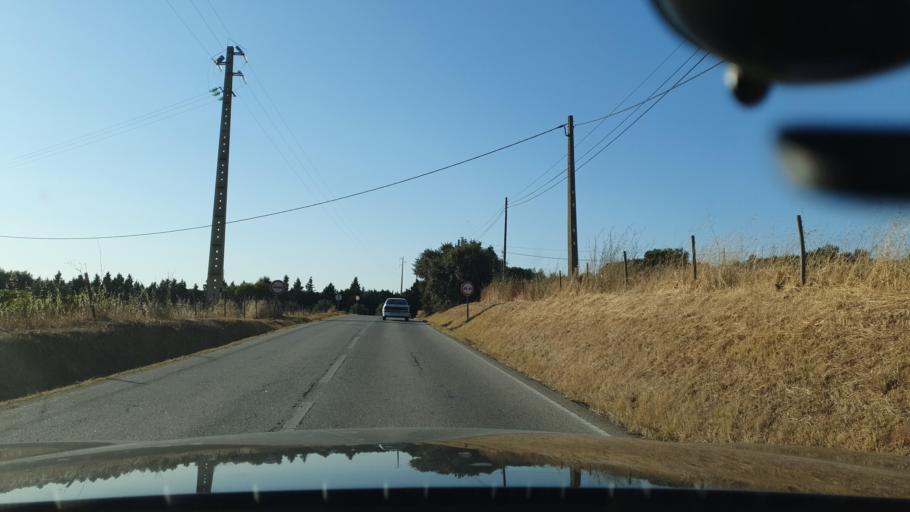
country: PT
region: Evora
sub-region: Estremoz
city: Estremoz
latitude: 38.8542
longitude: -7.6132
